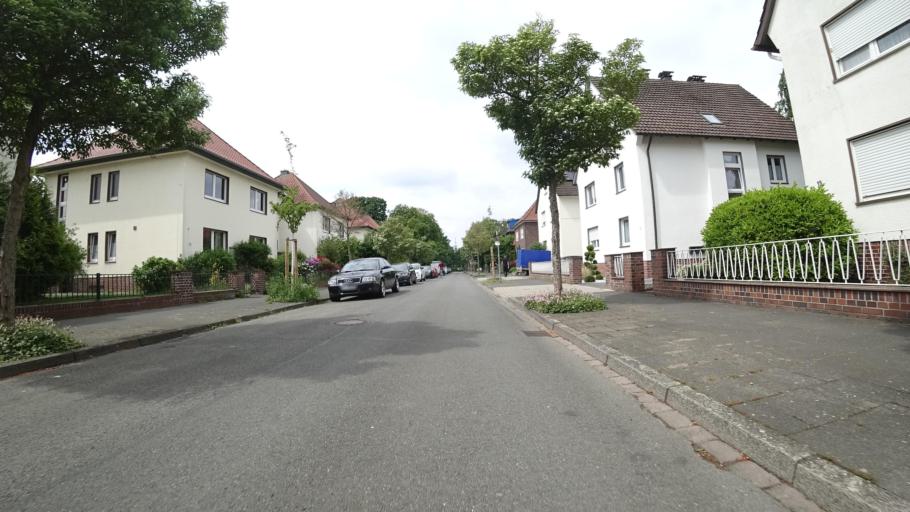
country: DE
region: North Rhine-Westphalia
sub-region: Regierungsbezirk Detmold
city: Guetersloh
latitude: 51.9067
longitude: 8.3974
